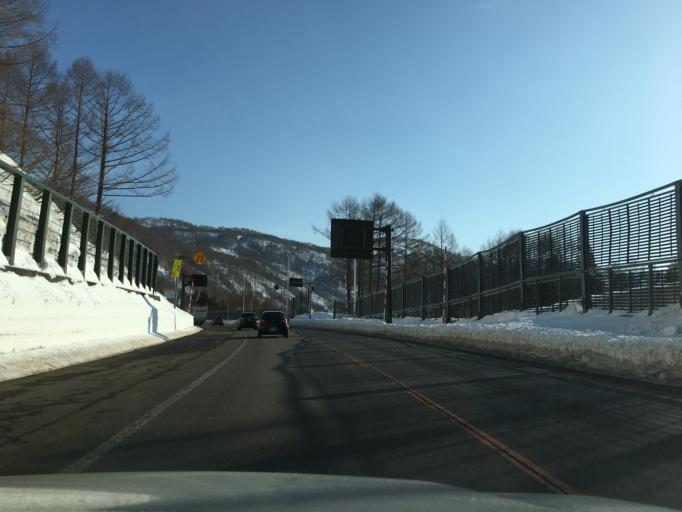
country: JP
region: Yamagata
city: Tsuruoka
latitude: 38.5259
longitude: 139.9492
